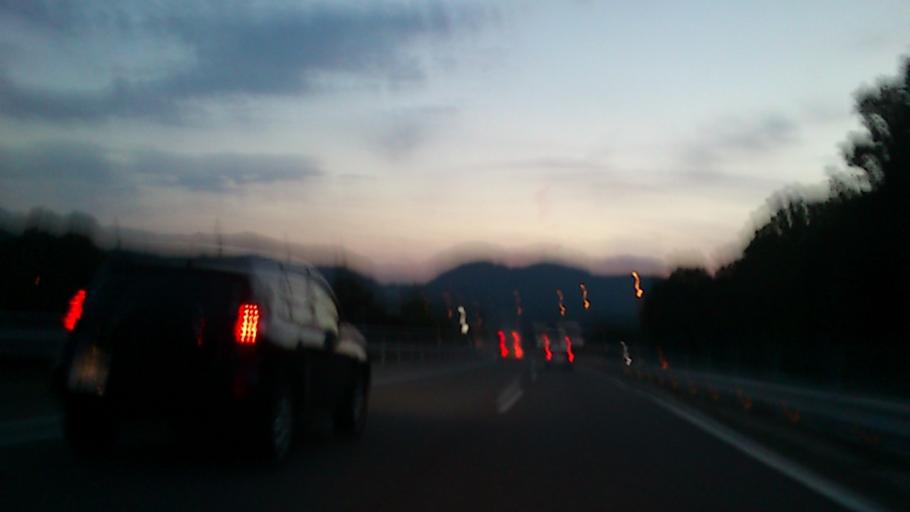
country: JP
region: Gifu
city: Tajimi
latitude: 35.3485
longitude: 137.1104
